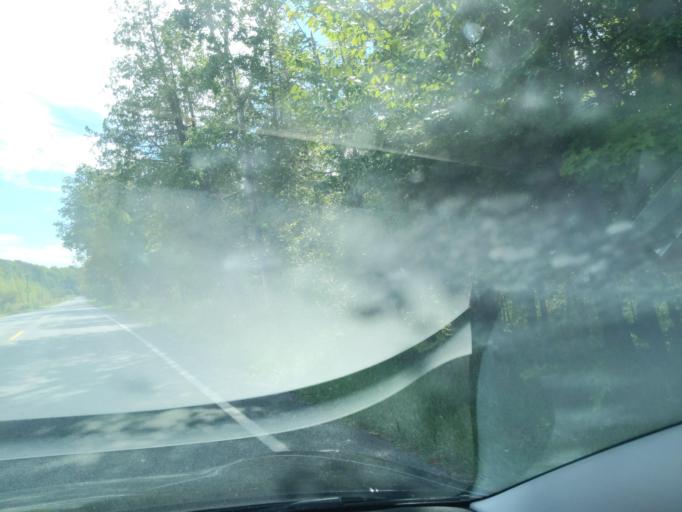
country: US
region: Michigan
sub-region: Antrim County
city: Bellaire
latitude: 45.0147
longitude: -85.2922
